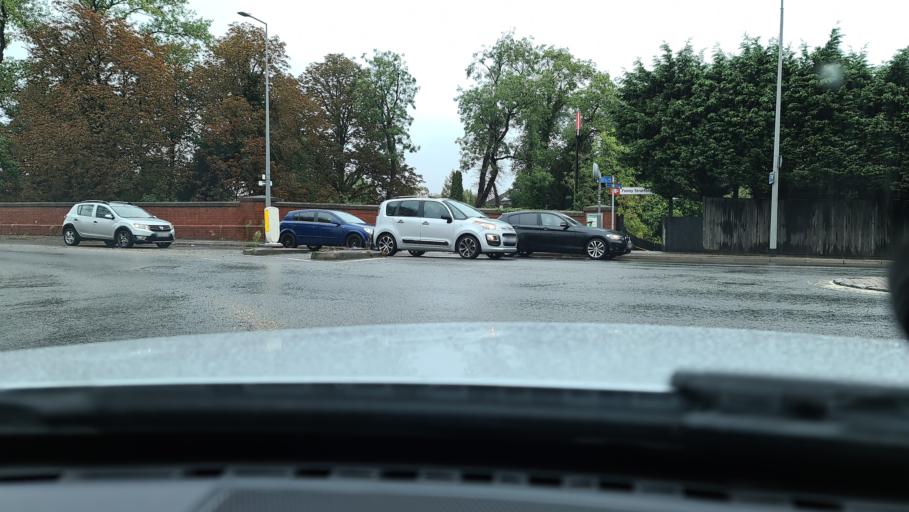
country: GB
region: England
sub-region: Milton Keynes
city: Water Eaton
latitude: 51.9996
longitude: -0.7194
